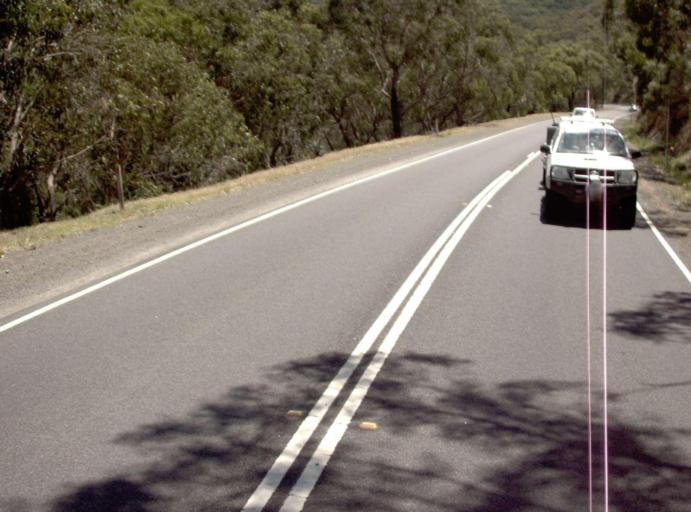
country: AU
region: Victoria
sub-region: Yarra Ranges
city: Tremont
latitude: -37.8923
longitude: 145.3243
